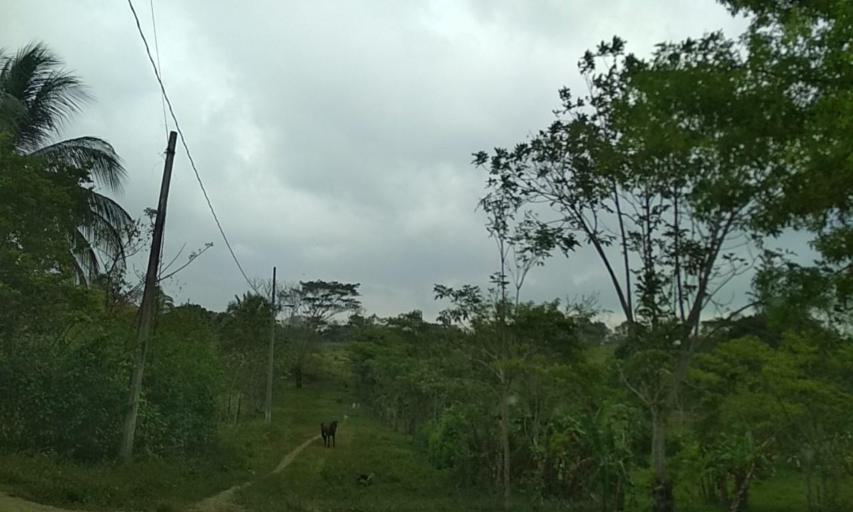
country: MX
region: Tabasco
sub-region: Huimanguillo
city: Francisco Rueda
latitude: 17.6580
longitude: -94.0986
